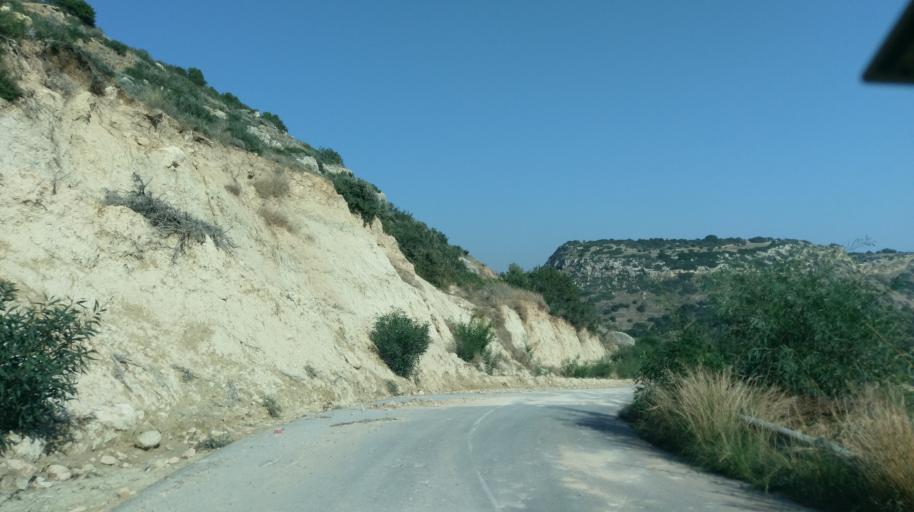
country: CY
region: Ammochostos
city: Leonarisso
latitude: 35.4931
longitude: 34.2245
